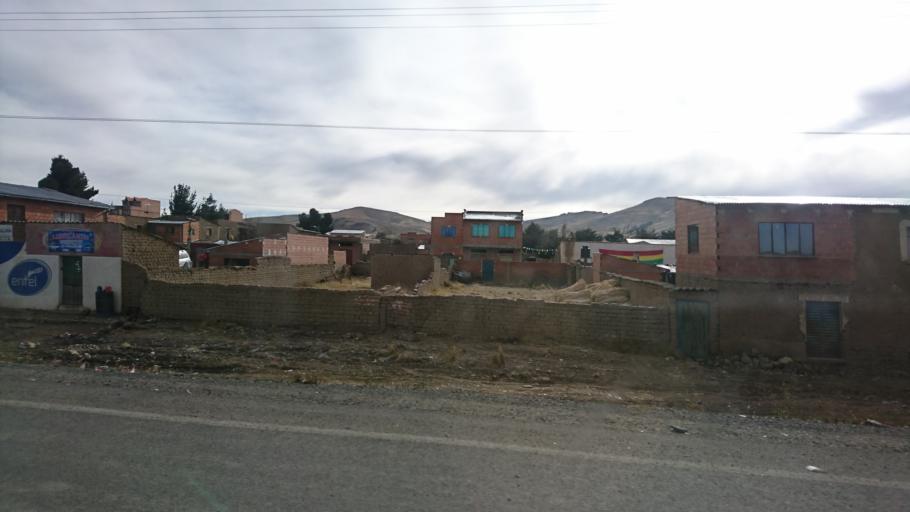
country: BO
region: La Paz
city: Batallas
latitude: -16.3786
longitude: -68.3785
